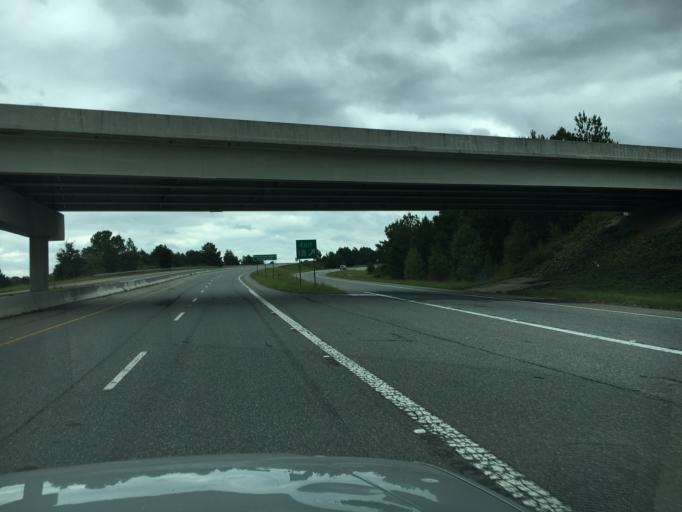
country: US
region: South Carolina
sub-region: Greenville County
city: Mauldin
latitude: 34.7527
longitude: -82.2922
